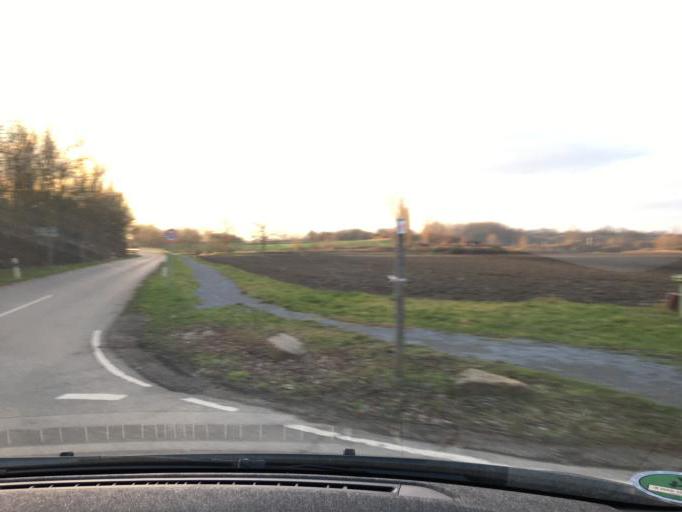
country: DE
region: North Rhine-Westphalia
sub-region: Regierungsbezirk Koln
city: Inden
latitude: 50.8532
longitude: 6.3603
